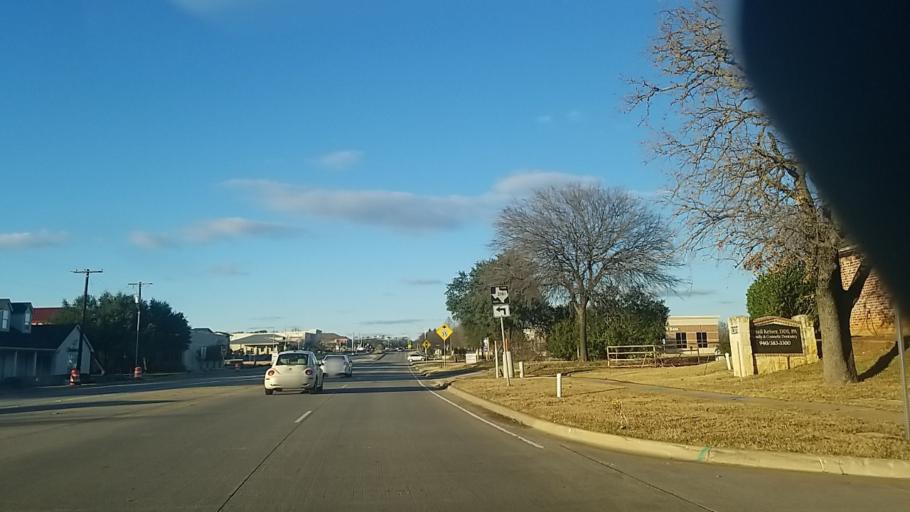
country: US
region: Texas
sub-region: Denton County
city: Denton
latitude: 33.1725
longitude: -97.1130
